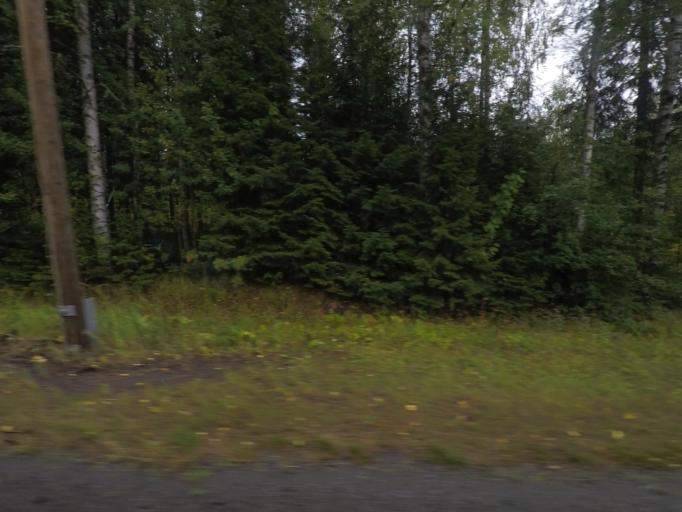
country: FI
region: Southern Savonia
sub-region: Pieksaemaeki
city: Joroinen
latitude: 62.1360
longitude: 27.8384
